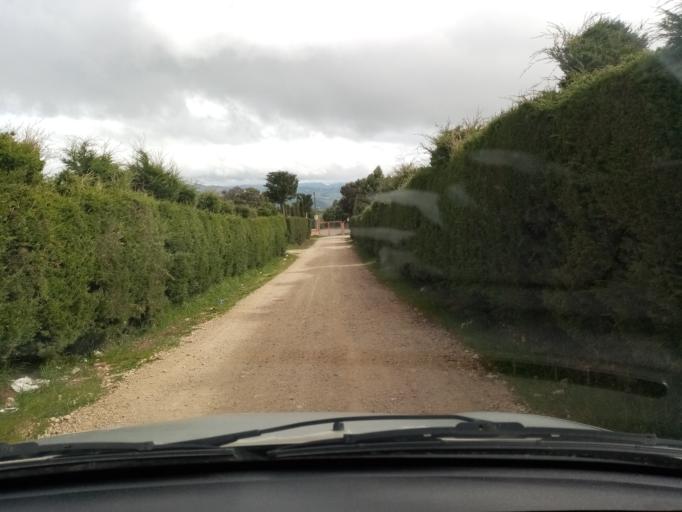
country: CO
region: Boyaca
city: Siachoque
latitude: 5.5483
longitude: -73.2993
